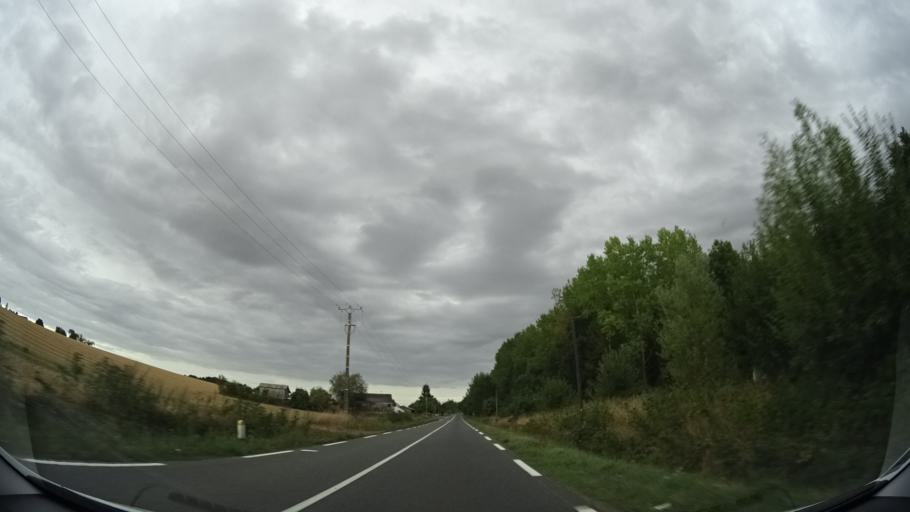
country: FR
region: Centre
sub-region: Departement du Loiret
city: Saint-Germain-des-Pres
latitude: 47.9510
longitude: 2.8567
